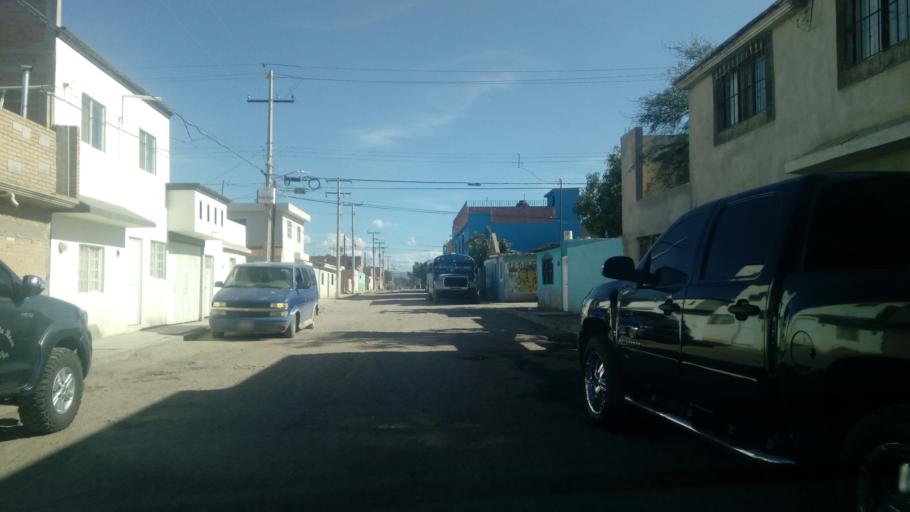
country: MX
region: Durango
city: Victoria de Durango
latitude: 24.0108
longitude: -104.6255
